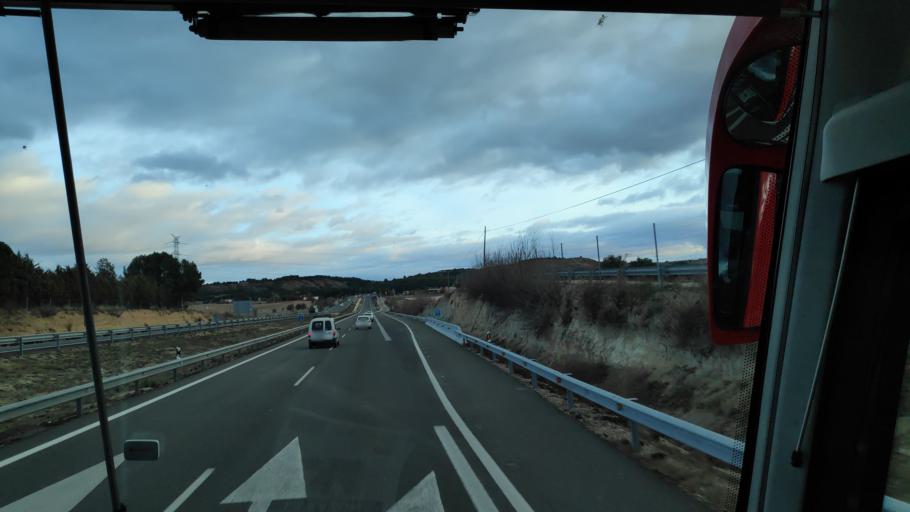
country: ES
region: Castille-La Mancha
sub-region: Provincia de Cuenca
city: Belinchon
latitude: 40.0391
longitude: -3.0505
